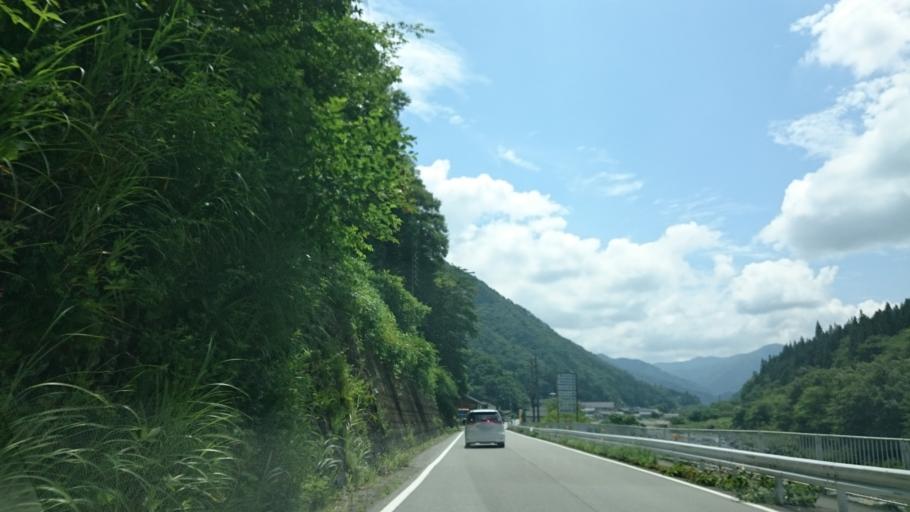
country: JP
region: Gifu
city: Takayama
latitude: 35.9284
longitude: 137.3060
